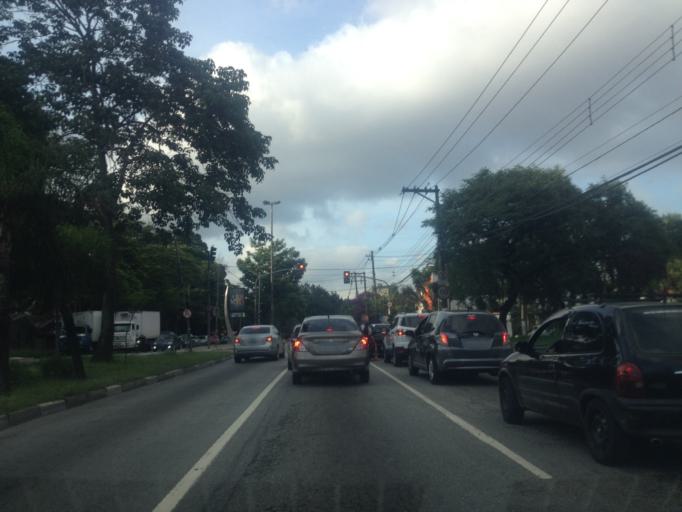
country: BR
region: Sao Paulo
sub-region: Diadema
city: Diadema
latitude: -23.7022
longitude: -46.7149
